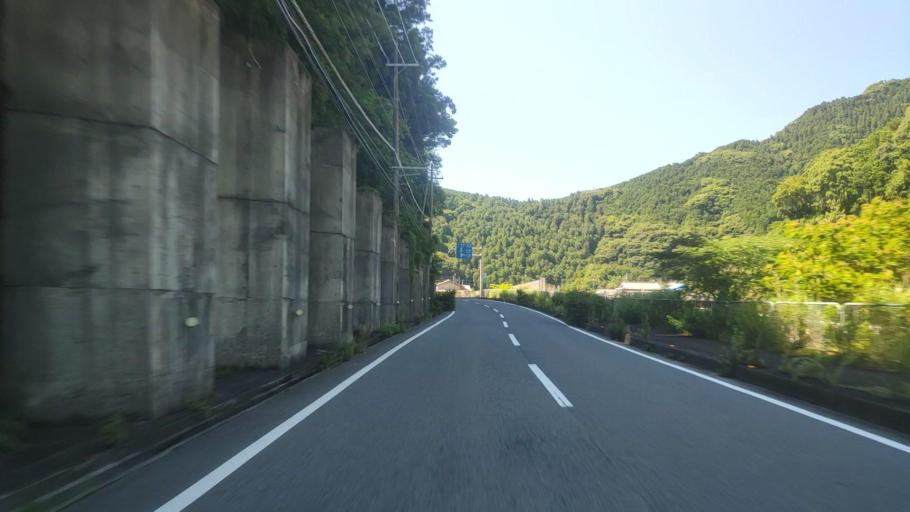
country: JP
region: Nara
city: Yoshino-cho
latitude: 34.3002
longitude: 135.9987
